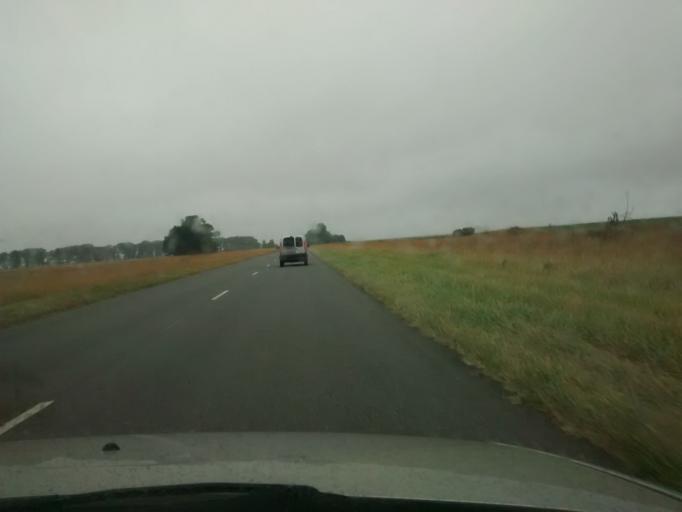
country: AR
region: Buenos Aires
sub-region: Partido de Ayacucho
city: Ayacucho
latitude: -37.4704
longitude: -58.4783
